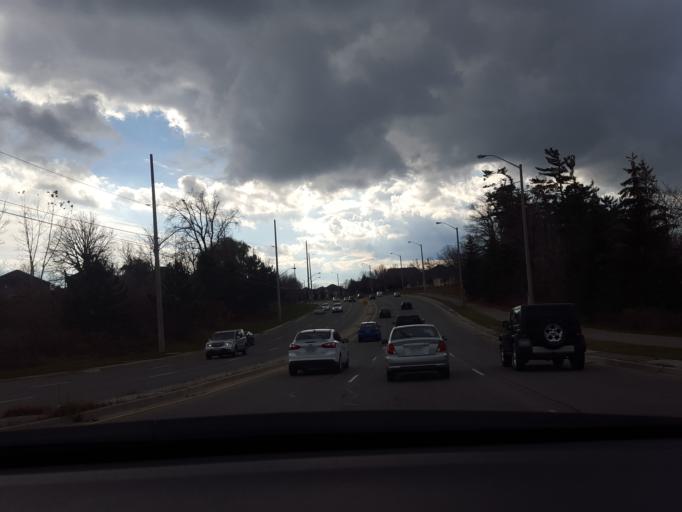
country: CA
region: Ontario
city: Brampton
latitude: 43.6294
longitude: -79.7405
